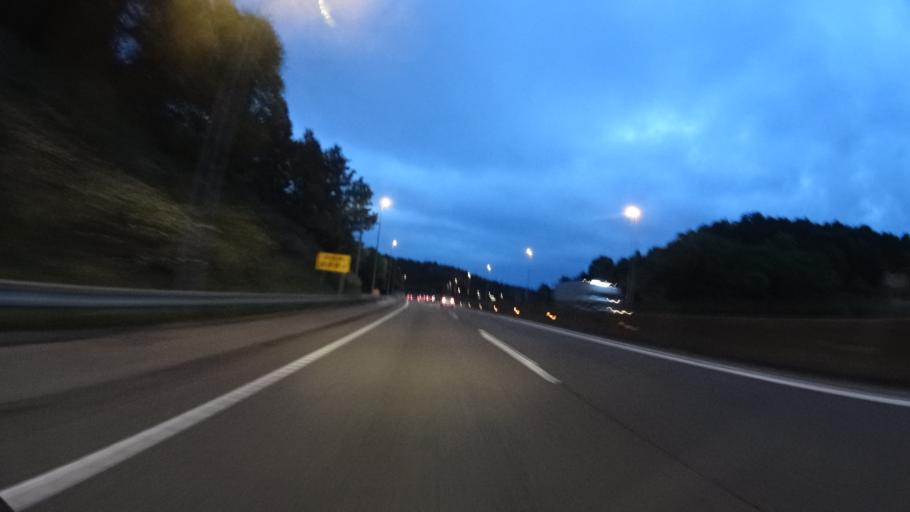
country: JP
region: Shiga Prefecture
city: Hikone
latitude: 35.1791
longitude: 136.2812
